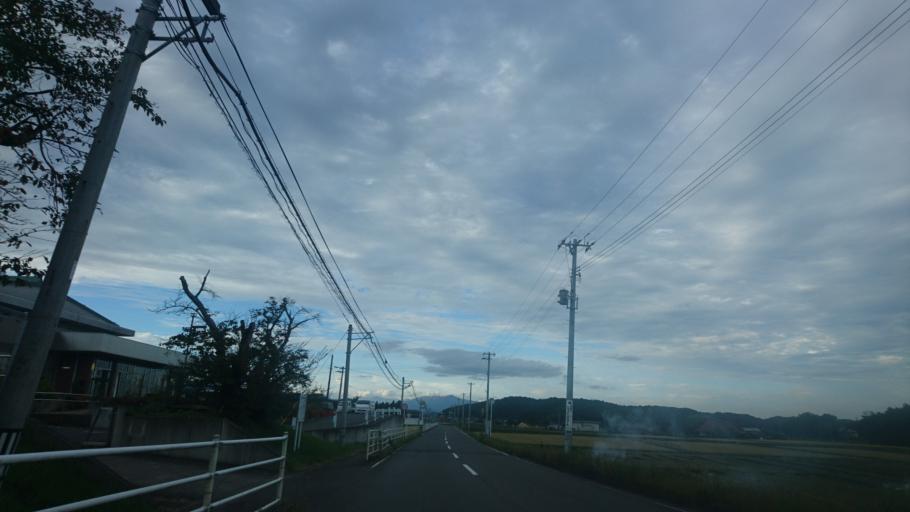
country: JP
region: Fukushima
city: Sukagawa
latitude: 37.3174
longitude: 140.2674
